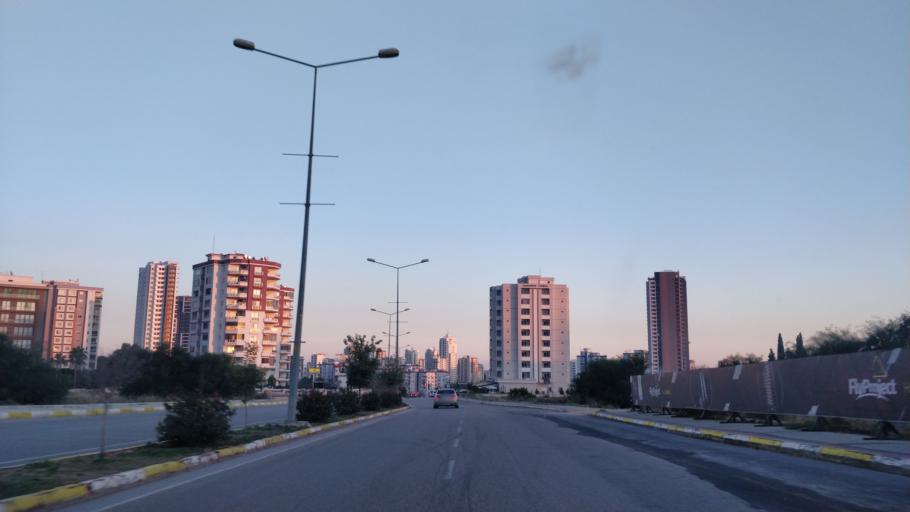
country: TR
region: Mersin
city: Mercin
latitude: 36.7996
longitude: 34.5741
